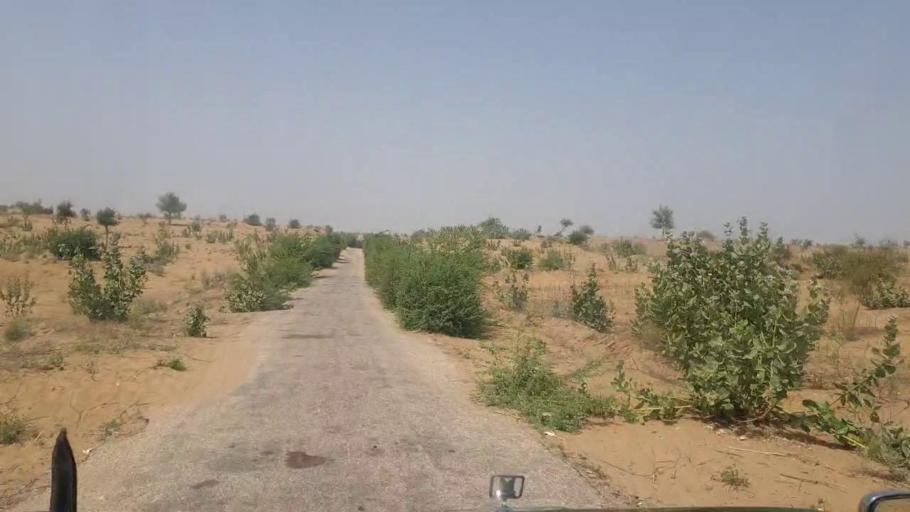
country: PK
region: Sindh
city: Islamkot
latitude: 25.1351
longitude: 70.2089
